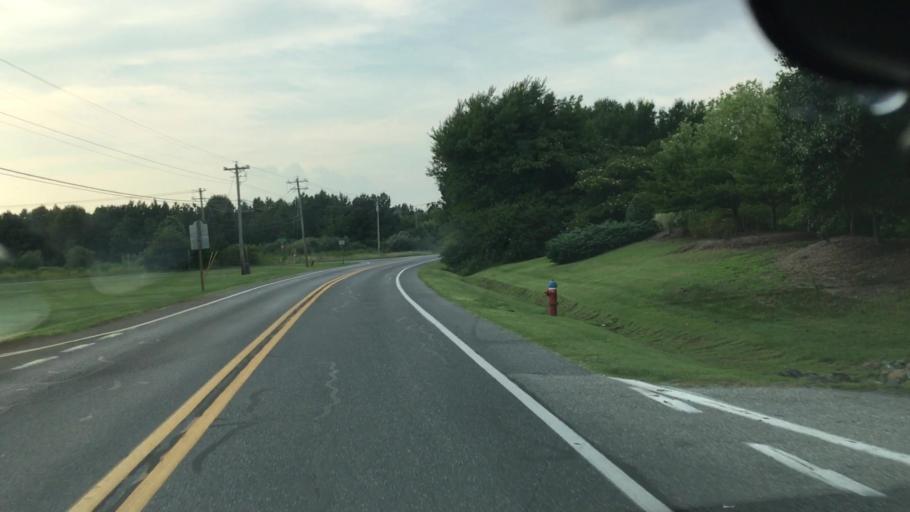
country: US
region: Delaware
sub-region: Sussex County
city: Ocean View
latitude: 38.5327
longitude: -75.0881
